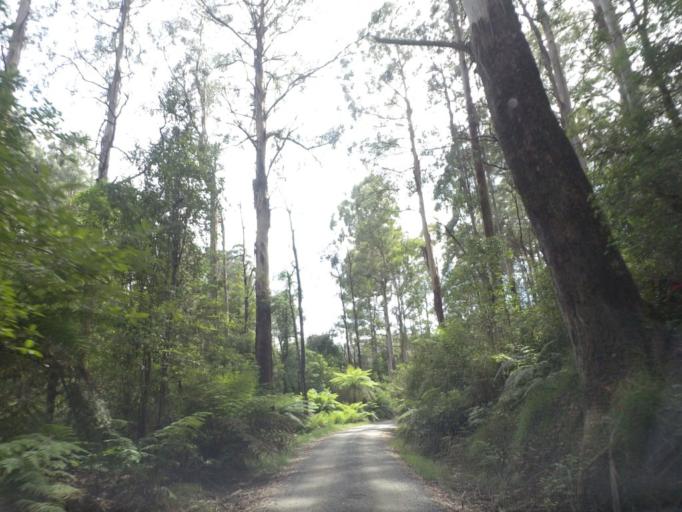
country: AU
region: Victoria
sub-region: Yarra Ranges
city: Healesville
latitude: -37.5285
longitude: 145.5195
